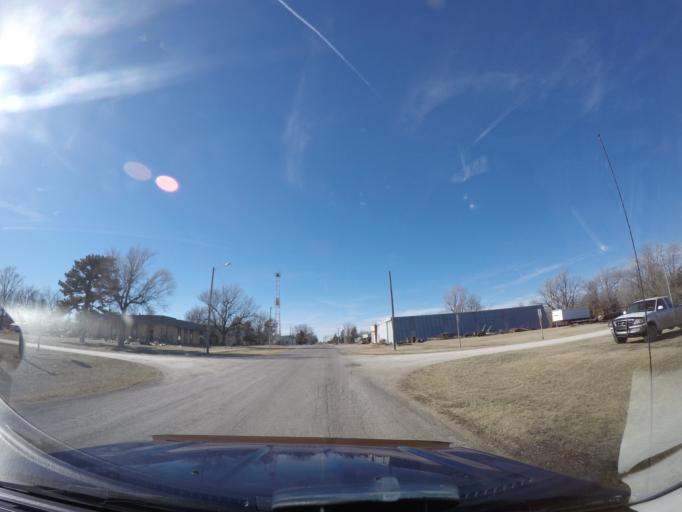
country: US
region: Kansas
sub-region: Dickinson County
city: Herington
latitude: 38.5660
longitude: -96.9657
